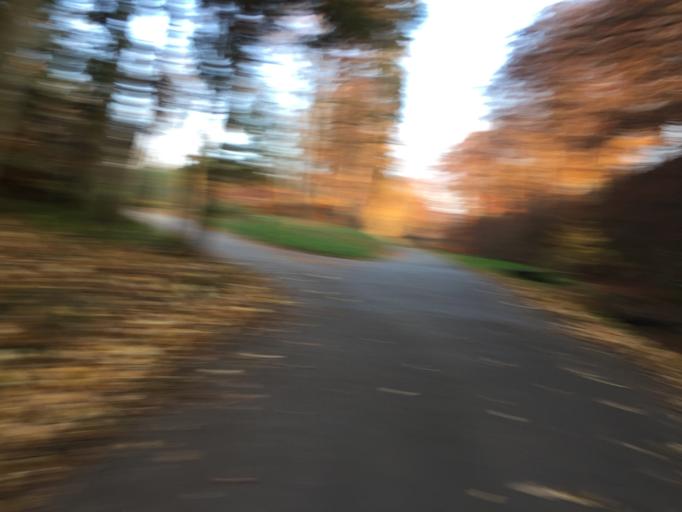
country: CH
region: Bern
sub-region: Bern-Mittelland District
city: Taegertschi
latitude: 46.8769
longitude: 7.5757
